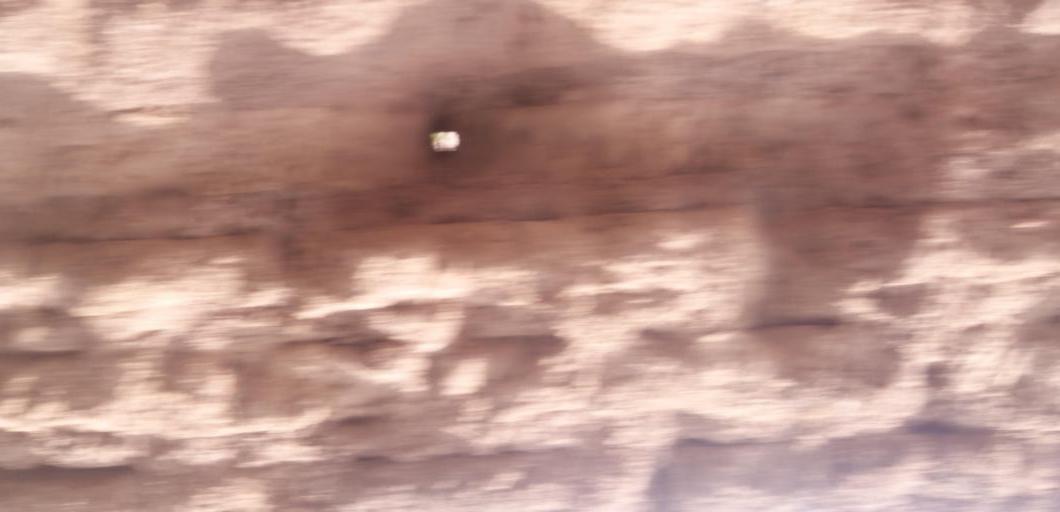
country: GT
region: Quetzaltenango
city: Quetzaltenango
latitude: 14.8295
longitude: -91.5294
